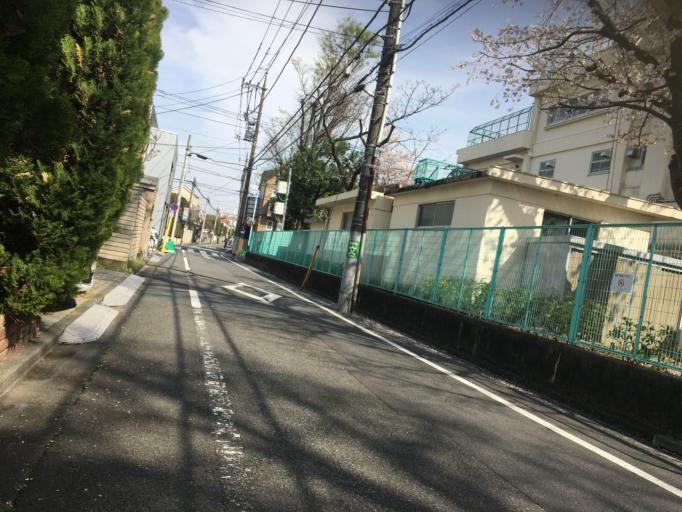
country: JP
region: Tokyo
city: Musashino
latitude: 35.7219
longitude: 139.6100
